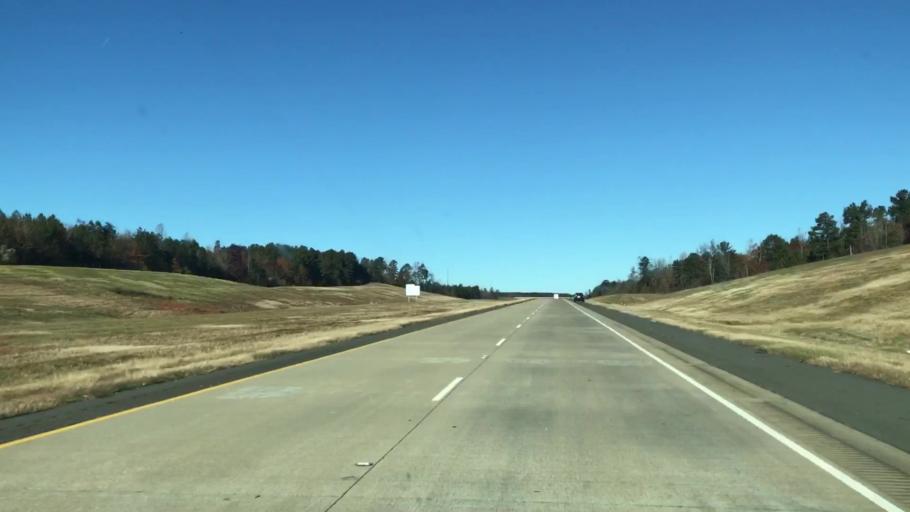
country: US
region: Louisiana
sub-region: Caddo Parish
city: Vivian
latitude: 32.9124
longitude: -93.8730
